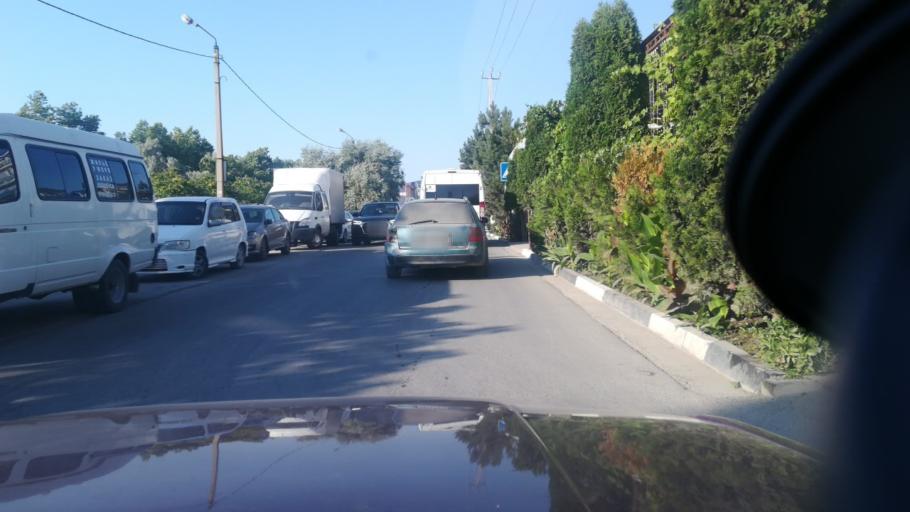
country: RU
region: Krasnodarskiy
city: Vityazevo
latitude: 44.9876
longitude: 37.2517
